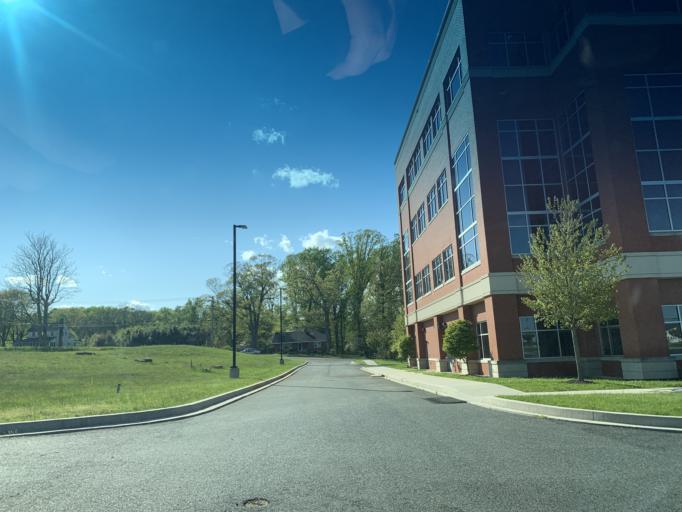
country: US
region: Maryland
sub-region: Harford County
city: Aberdeen
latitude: 39.5318
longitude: -76.1921
